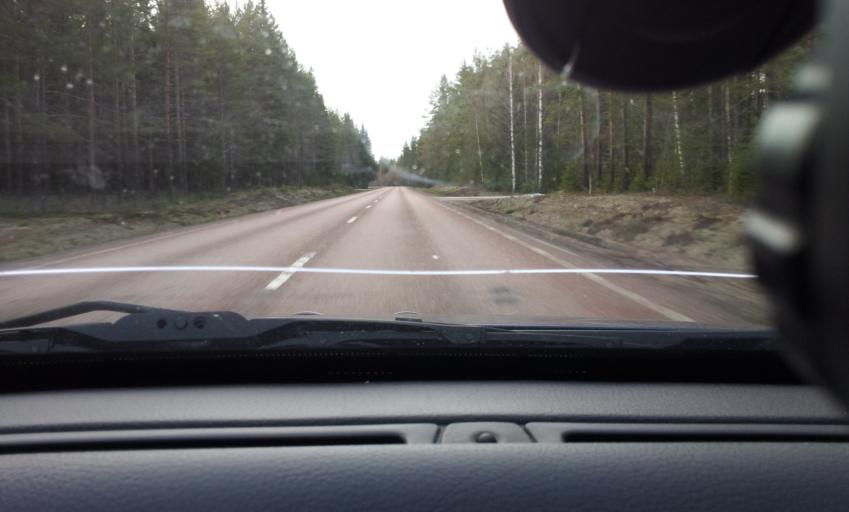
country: SE
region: Gaevleborg
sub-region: Ljusdals Kommun
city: Farila
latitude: 61.8810
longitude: 15.7104
